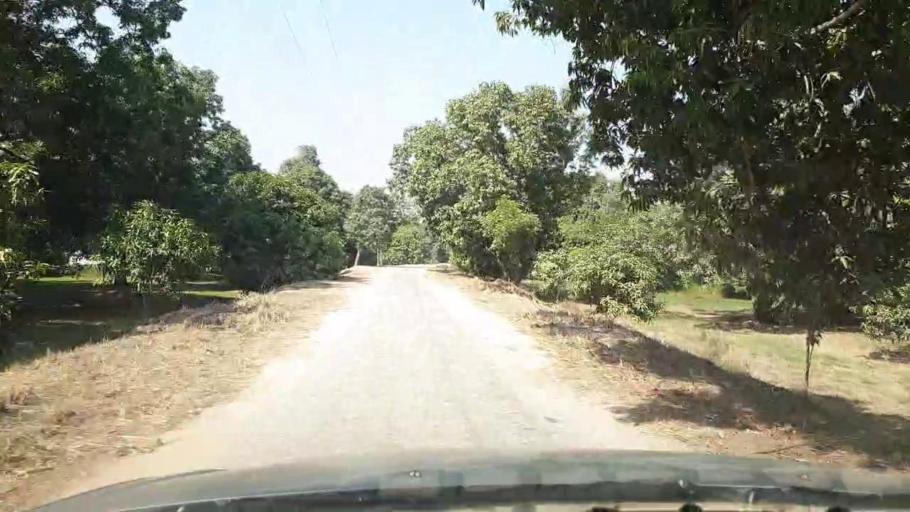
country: PK
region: Sindh
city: Tando Jam
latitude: 25.3626
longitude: 68.5138
